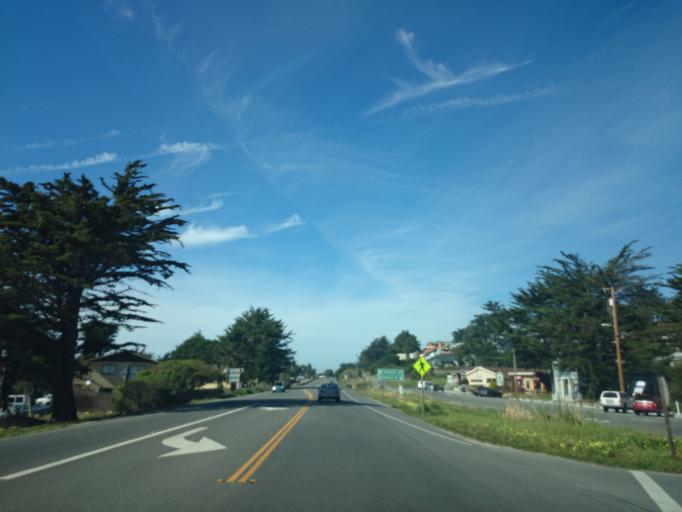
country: US
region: California
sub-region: San Mateo County
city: Moss Beach
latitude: 37.5275
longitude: -122.5134
